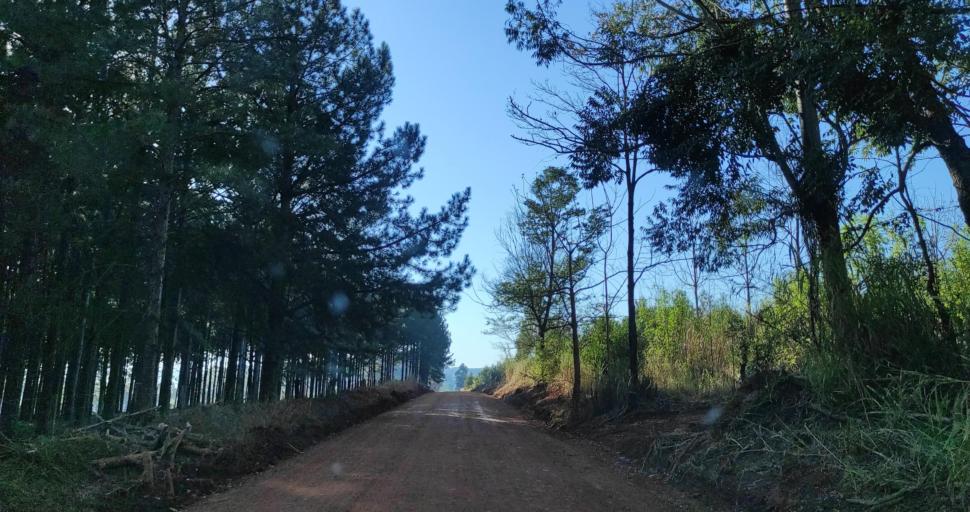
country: AR
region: Misiones
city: Capiovi
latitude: -26.8801
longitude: -55.0423
